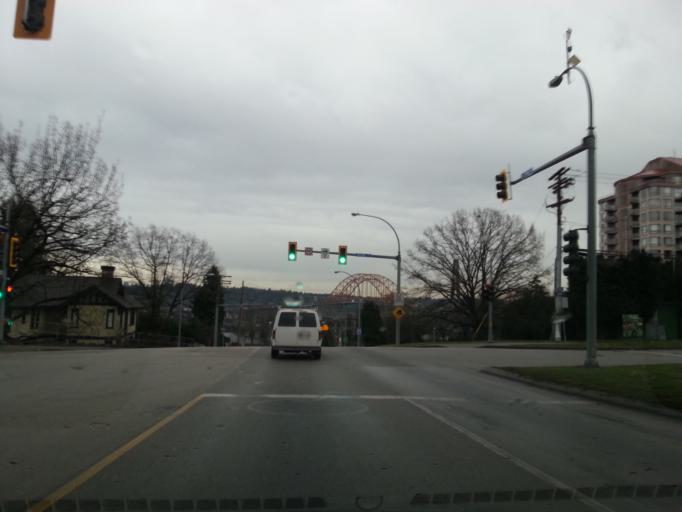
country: CA
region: British Columbia
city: New Westminster
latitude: 49.2122
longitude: -122.8992
